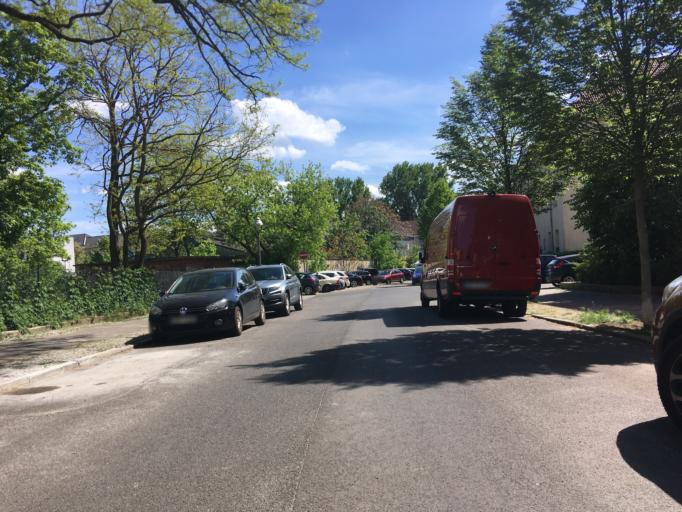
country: DE
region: Berlin
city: Berlin Koepenick
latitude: 52.4566
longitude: 13.5856
